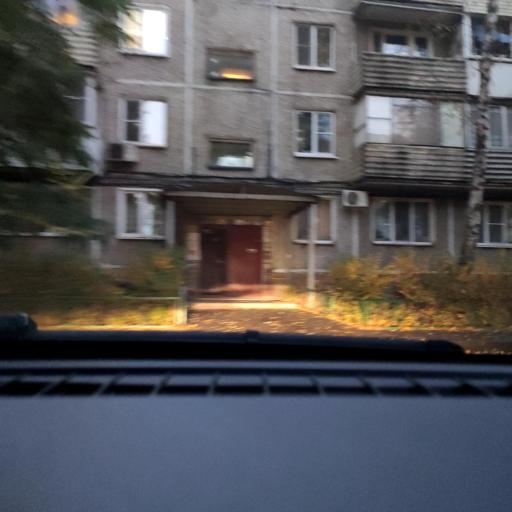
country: RU
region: Voronezj
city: Voronezh
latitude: 51.6953
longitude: 39.2584
